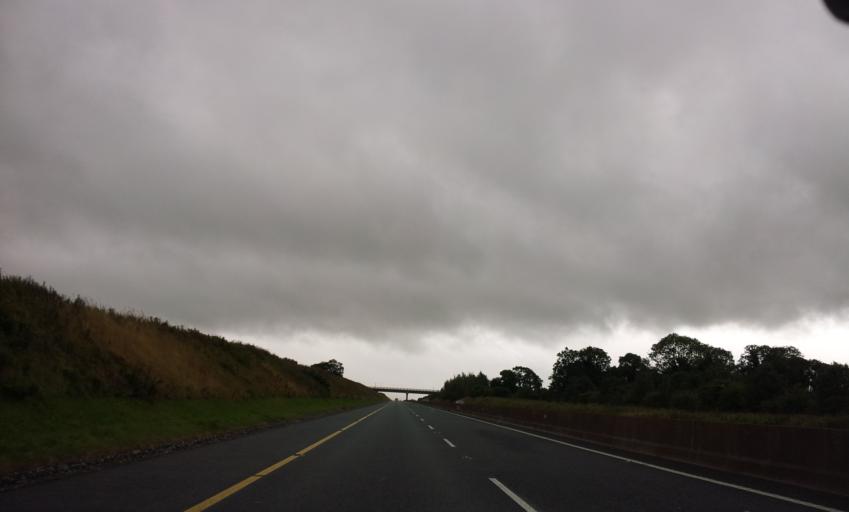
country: IE
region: Munster
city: Cashel
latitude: 52.4556
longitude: -7.9079
